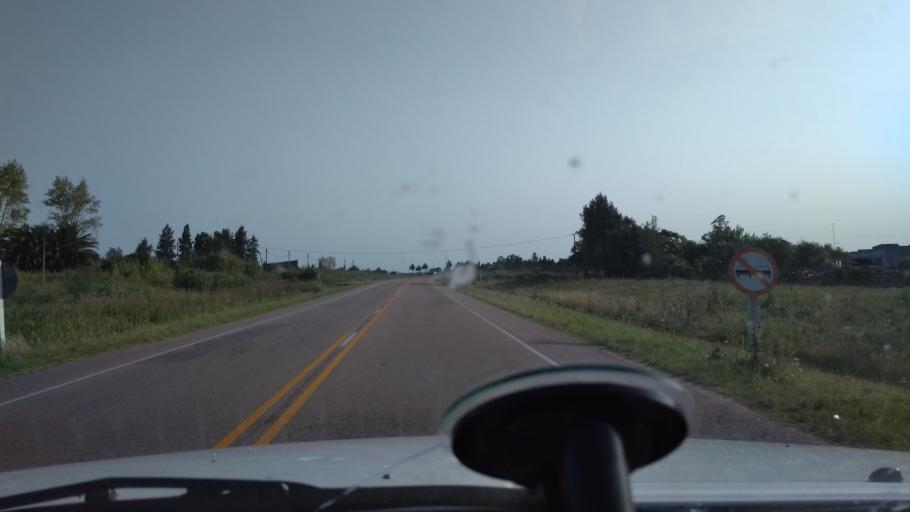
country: UY
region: Canelones
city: Sauce
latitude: -34.6585
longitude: -56.0558
